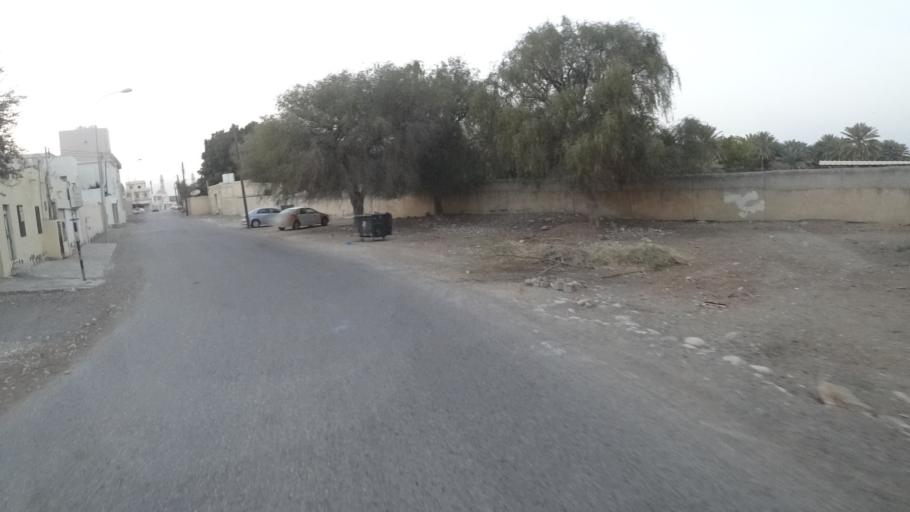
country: OM
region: Ash Sharqiyah
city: Sur
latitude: 22.5412
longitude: 59.4873
